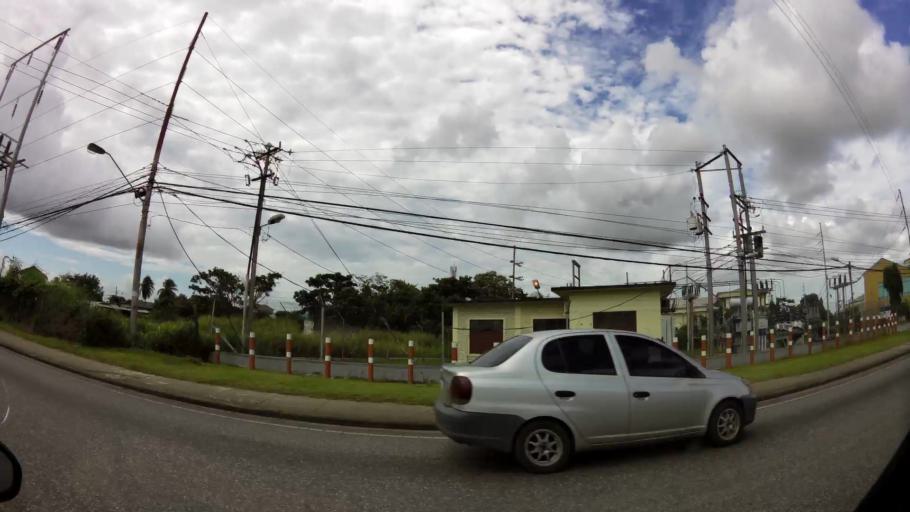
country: TT
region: Chaguanas
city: Chaguanas
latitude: 10.5106
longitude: -61.4077
